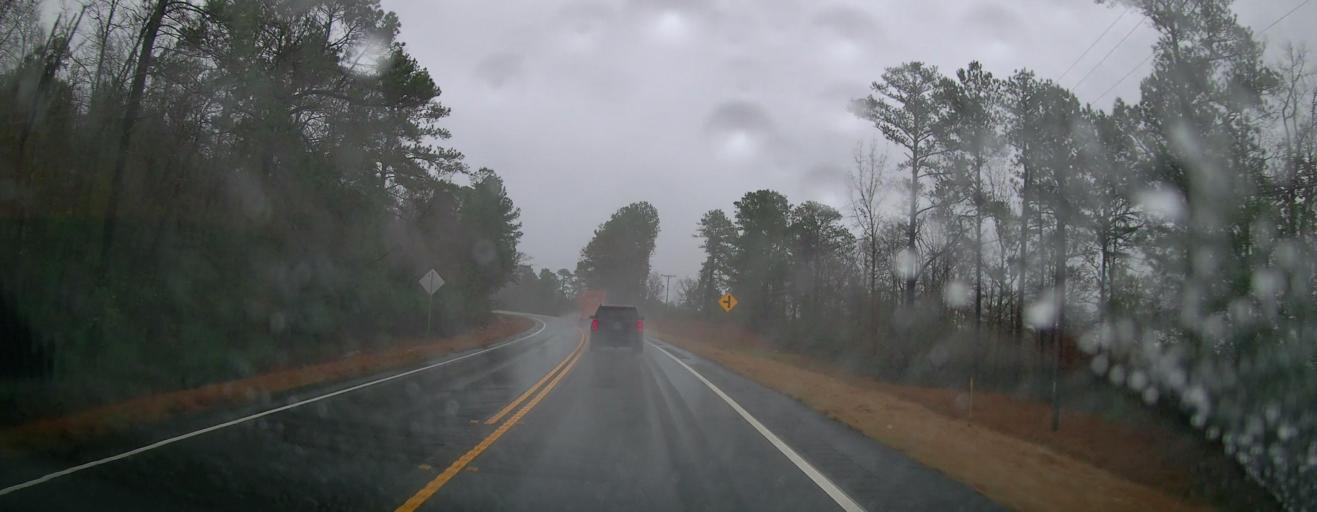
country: US
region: Georgia
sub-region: Putnam County
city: Eatonton
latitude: 33.2634
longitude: -83.4157
